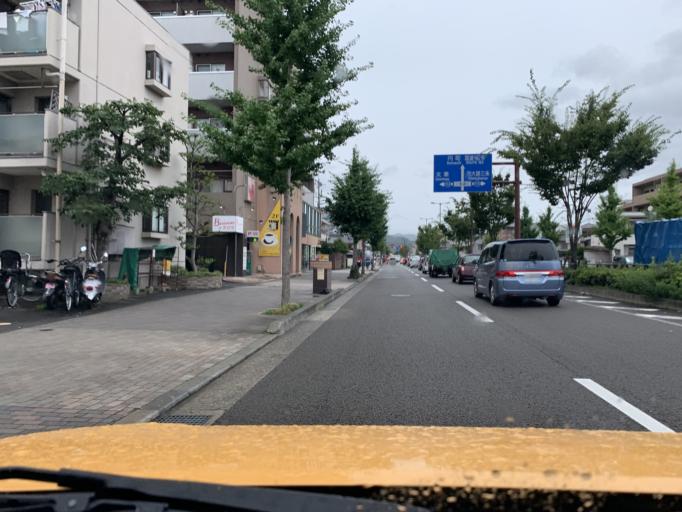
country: JP
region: Kyoto
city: Kyoto
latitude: 35.0065
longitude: 135.7195
